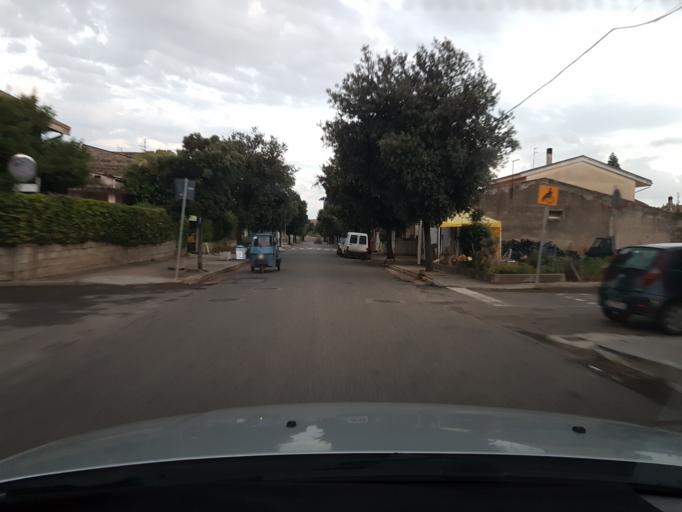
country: IT
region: Sardinia
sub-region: Provincia di Oristano
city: Tramatza
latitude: 40.0005
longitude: 8.6497
